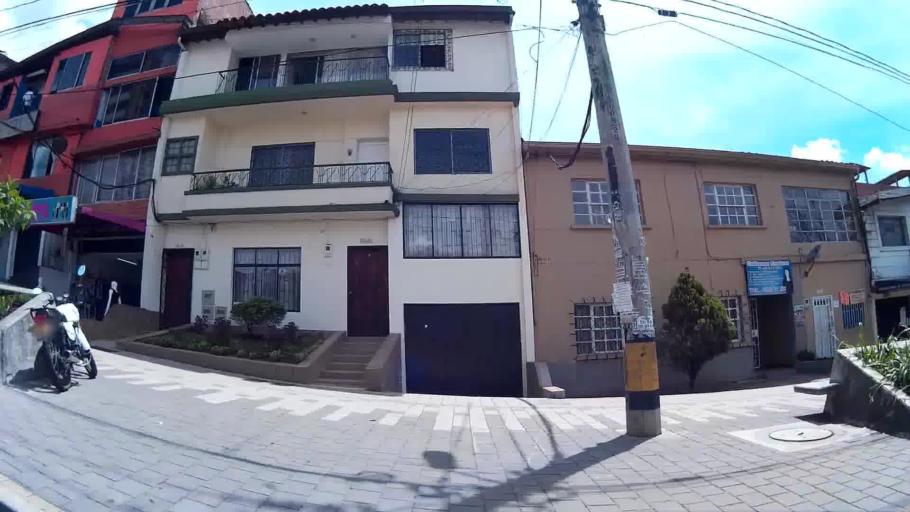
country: CO
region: Antioquia
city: Medellin
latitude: 6.2559
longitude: -75.6183
